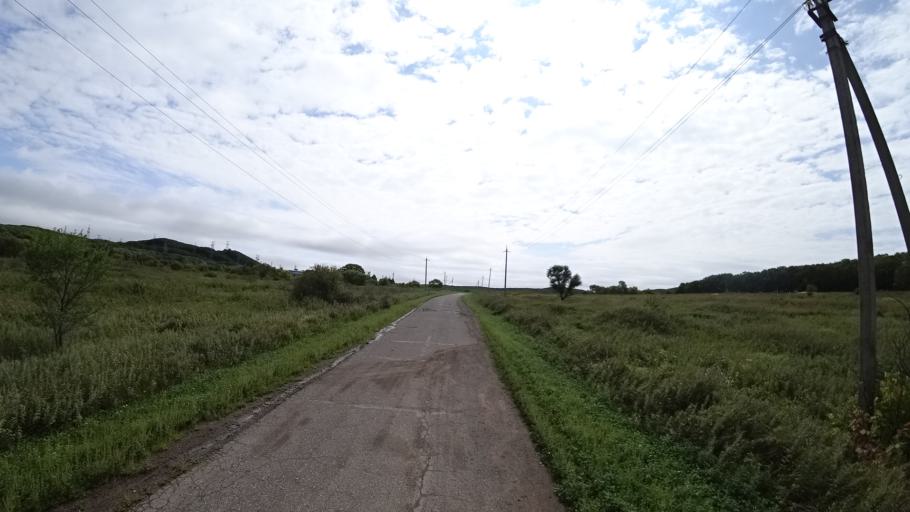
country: RU
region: Primorskiy
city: Lyalichi
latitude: 44.1342
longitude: 132.3879
